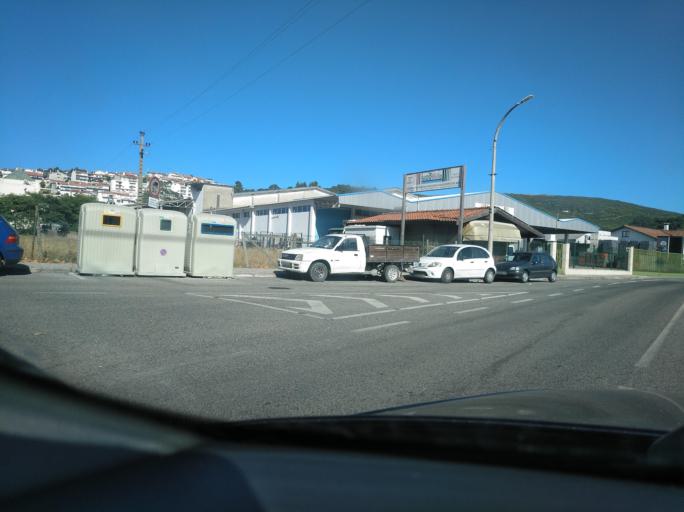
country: PT
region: Leiria
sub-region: Porto de Mos
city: Porto de Mos
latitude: 39.5979
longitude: -8.8189
